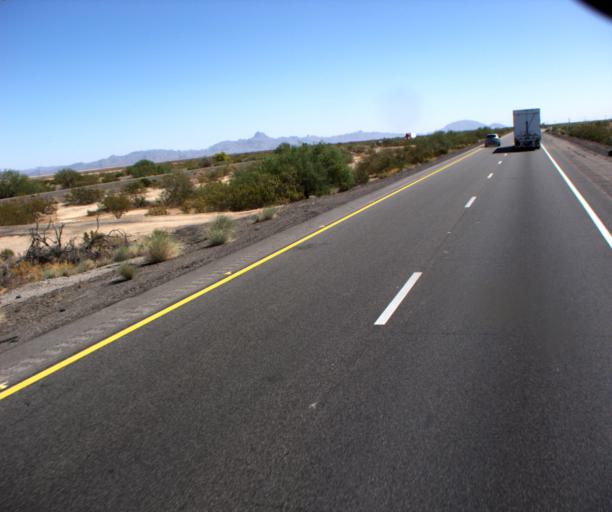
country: US
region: Arizona
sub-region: La Paz County
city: Salome
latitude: 33.5684
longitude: -113.3511
